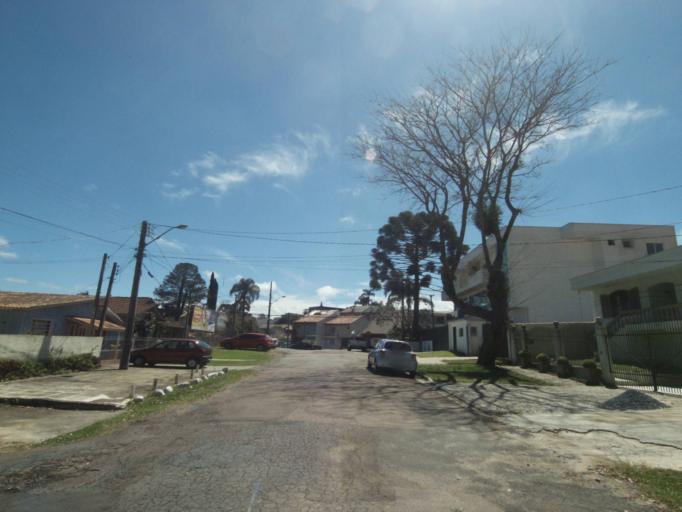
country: BR
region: Parana
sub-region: Curitiba
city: Curitiba
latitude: -25.3904
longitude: -49.2621
